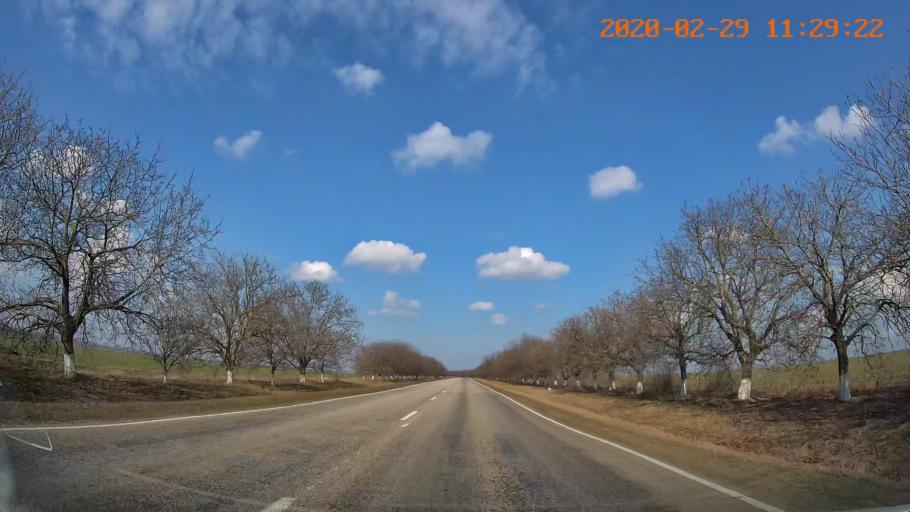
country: MD
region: Telenesti
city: Cocieri
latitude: 47.4934
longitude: 29.1261
